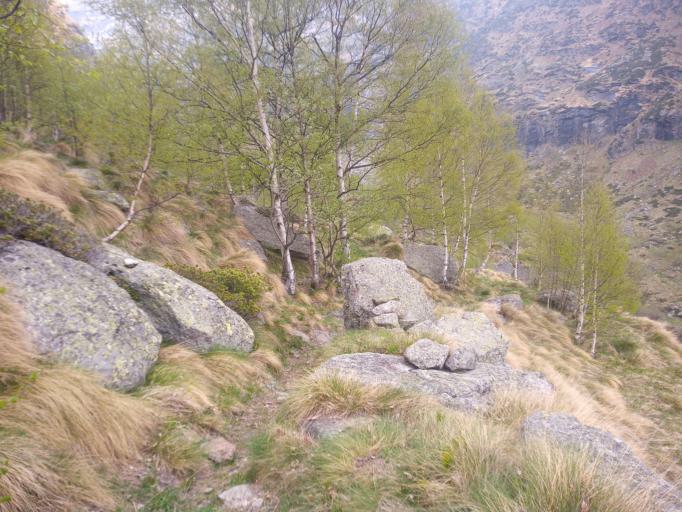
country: IT
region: Piedmont
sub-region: Provincia di Torino
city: Noasca
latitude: 45.4662
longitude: 7.3213
